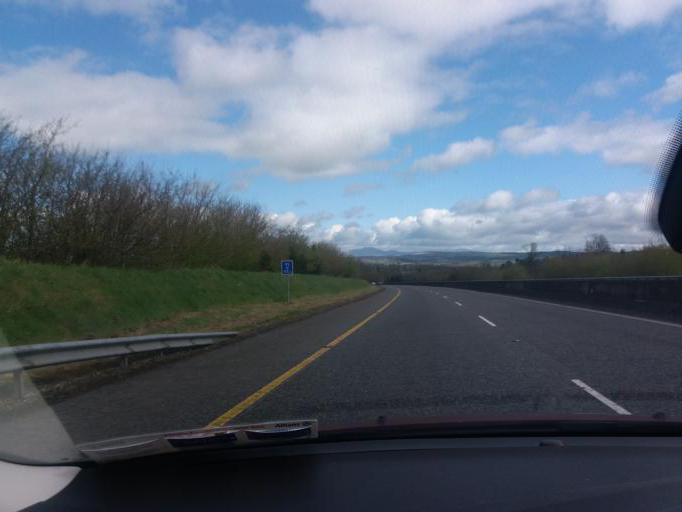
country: IE
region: Munster
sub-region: County Cork
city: Fermoy
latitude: 52.1284
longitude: -8.2606
